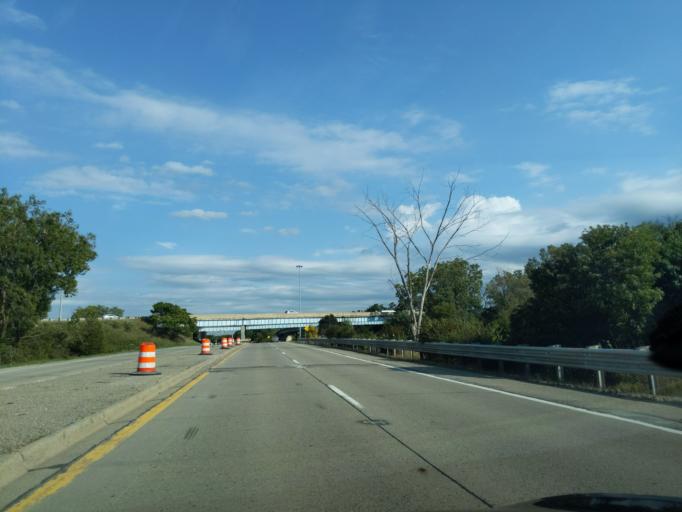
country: US
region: Michigan
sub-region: Ingham County
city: East Lansing
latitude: 42.7209
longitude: -84.5068
